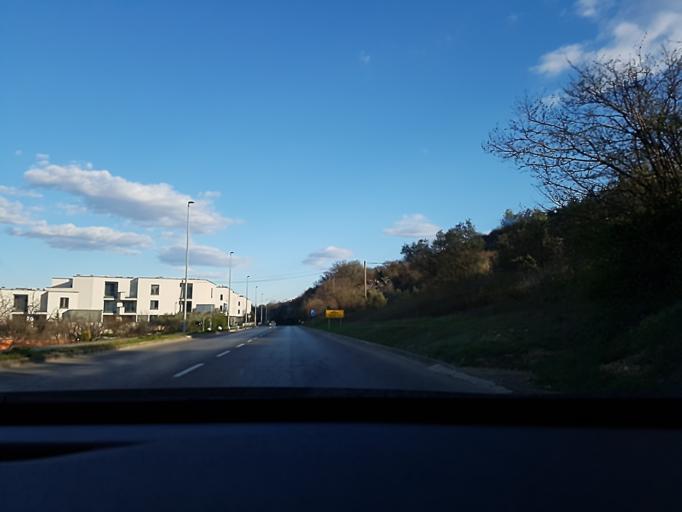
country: SI
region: Koper-Capodistria
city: Koper
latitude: 45.5416
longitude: 13.6980
